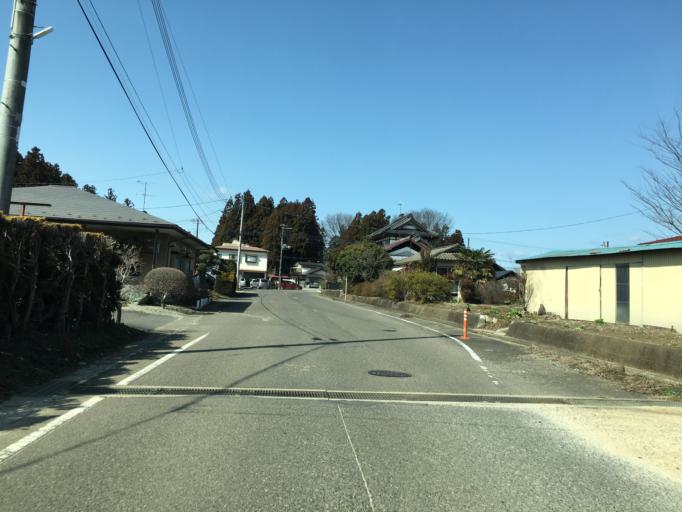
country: JP
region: Fukushima
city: Ishikawa
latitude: 37.1277
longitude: 140.2727
